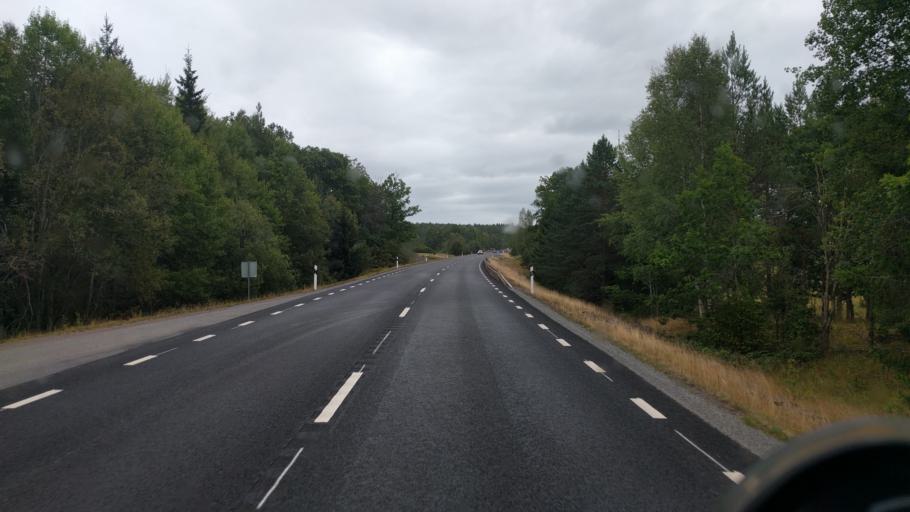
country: SE
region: Kalmar
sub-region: Vasterviks Kommun
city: Ankarsrum
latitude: 57.7245
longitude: 16.3921
